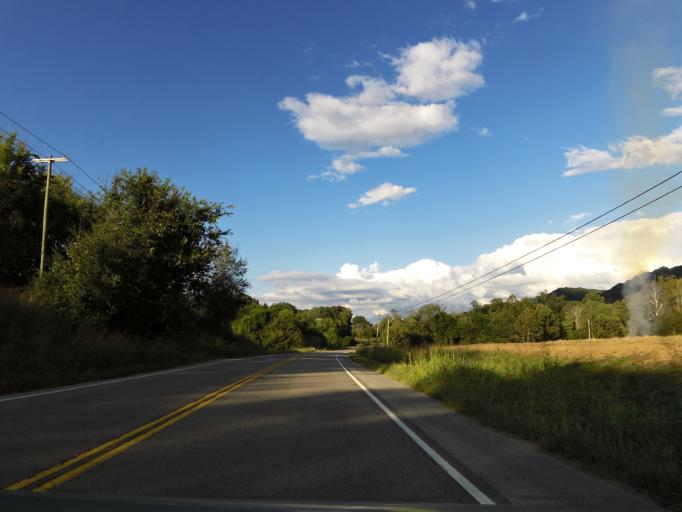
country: US
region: Tennessee
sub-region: Grainger County
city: Blaine
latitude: 36.2117
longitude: -83.6506
